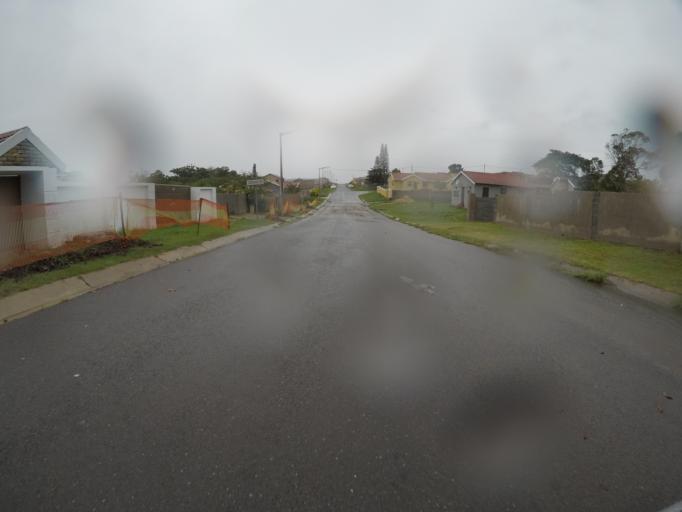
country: ZA
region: Eastern Cape
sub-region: Buffalo City Metropolitan Municipality
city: East London
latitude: -32.9937
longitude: 27.8410
